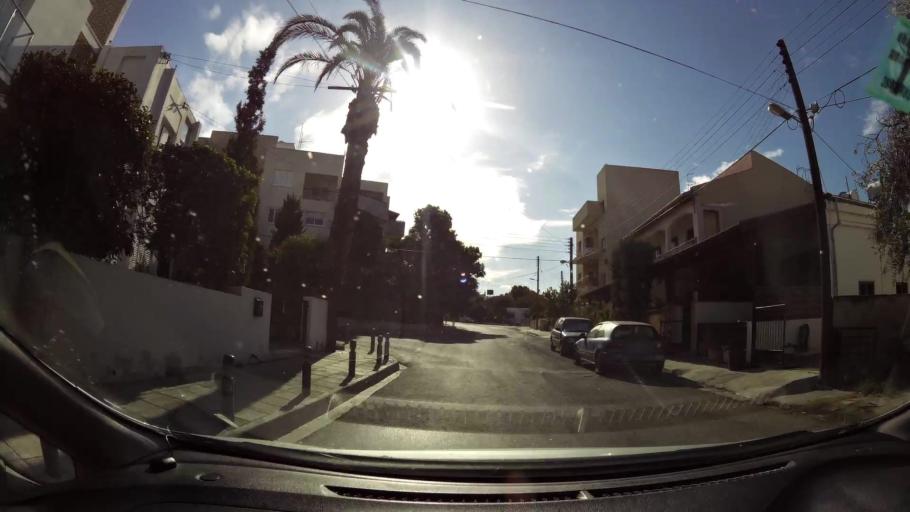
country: CY
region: Lefkosia
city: Nicosia
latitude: 35.1345
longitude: 33.3470
